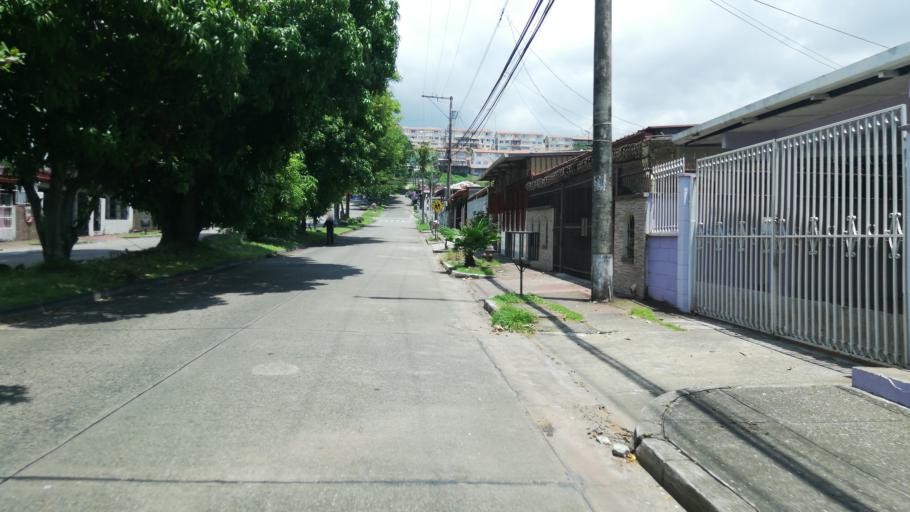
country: PA
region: Panama
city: San Miguelito
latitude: 9.0594
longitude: -79.4569
